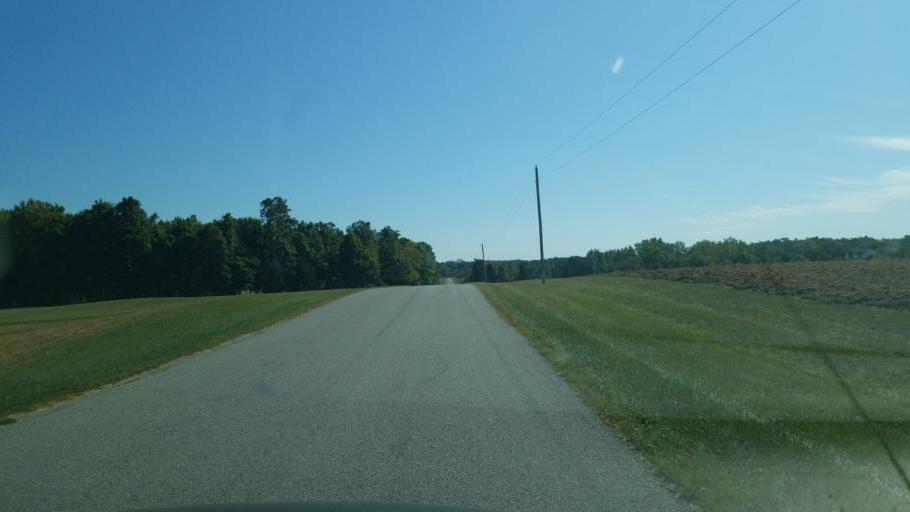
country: US
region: Ohio
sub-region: Champaign County
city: Mechanicsburg
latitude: 40.1260
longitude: -83.6003
